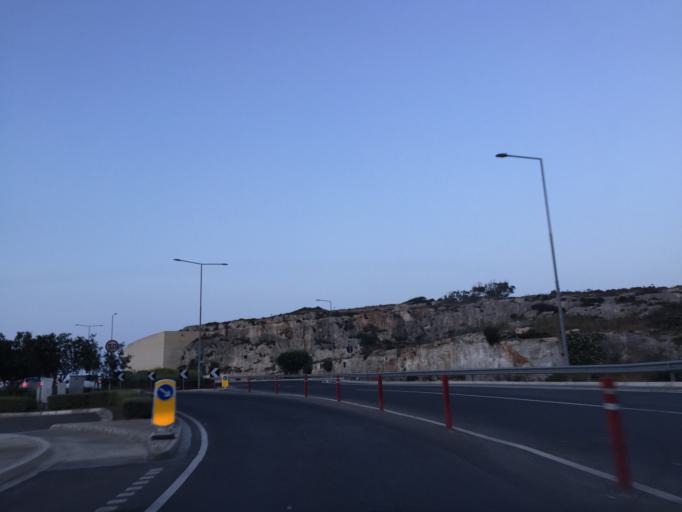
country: MT
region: Saint Paul's Bay
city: San Pawl il-Bahar
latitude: 35.9486
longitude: 14.4284
